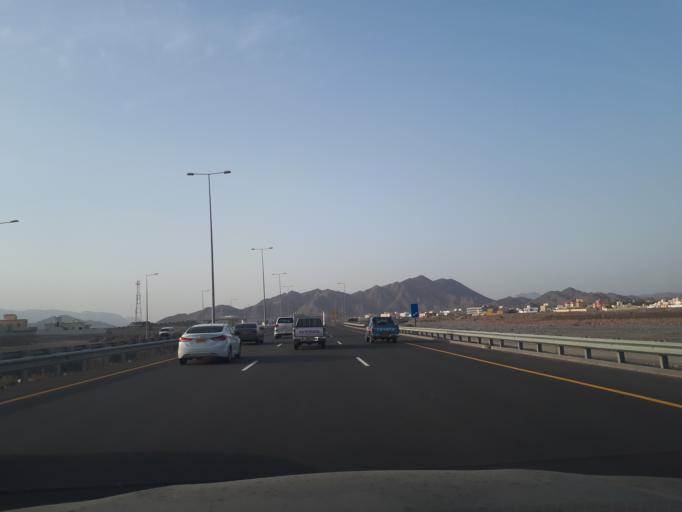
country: OM
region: Muhafazat ad Dakhiliyah
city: Bidbid
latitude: 23.3223
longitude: 58.1156
